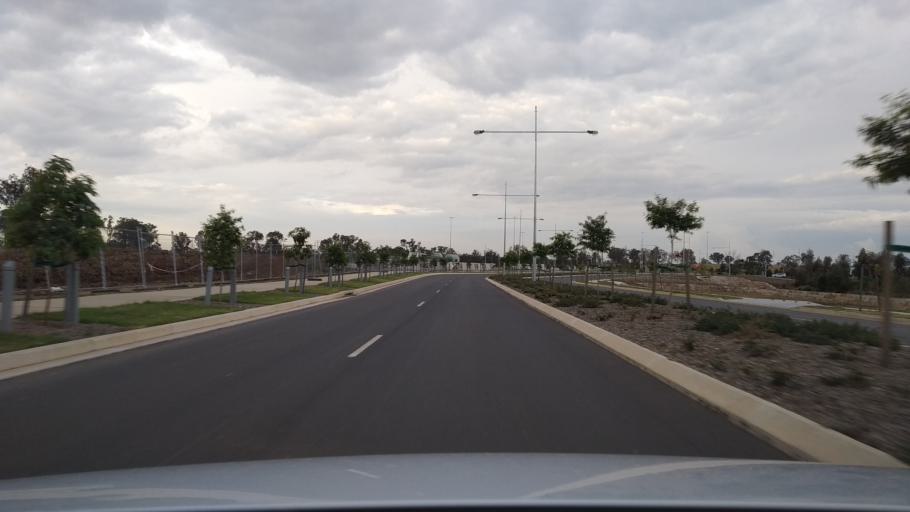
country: AU
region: New South Wales
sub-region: Camden
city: Narellan
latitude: -33.9954
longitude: 150.7317
